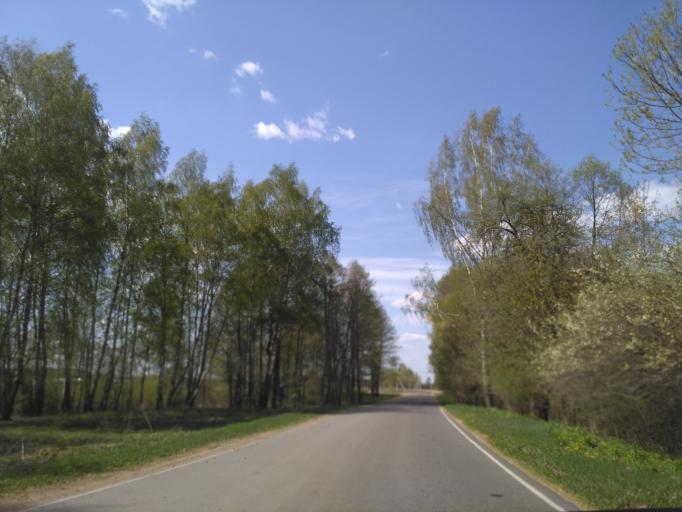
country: BY
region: Minsk
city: Narach
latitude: 54.9639
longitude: 26.6426
